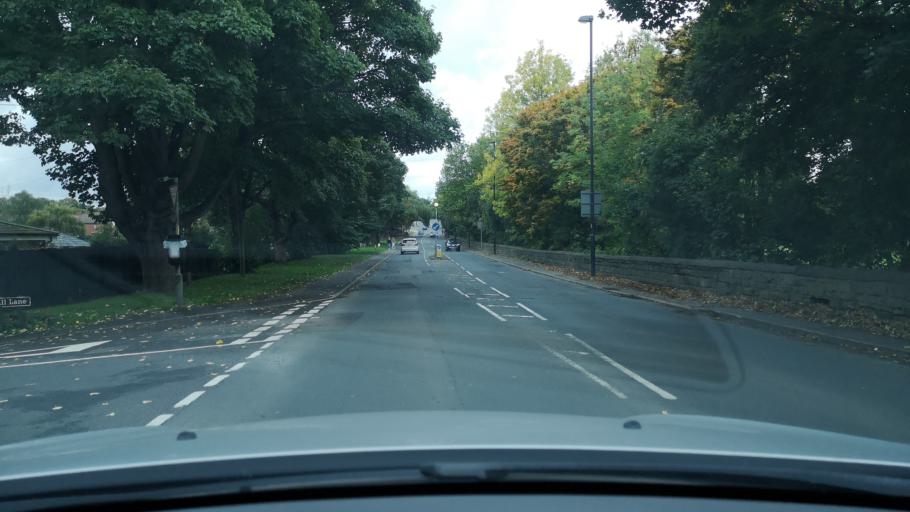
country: GB
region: England
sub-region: City and Borough of Wakefield
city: Low Ackworth
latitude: 53.6471
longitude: -1.3326
